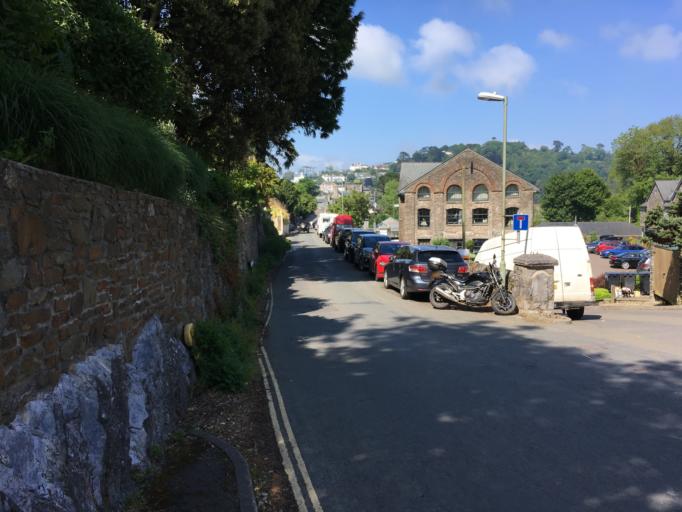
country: GB
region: England
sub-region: Devon
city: Dartmouth
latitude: 50.3414
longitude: -3.5748
